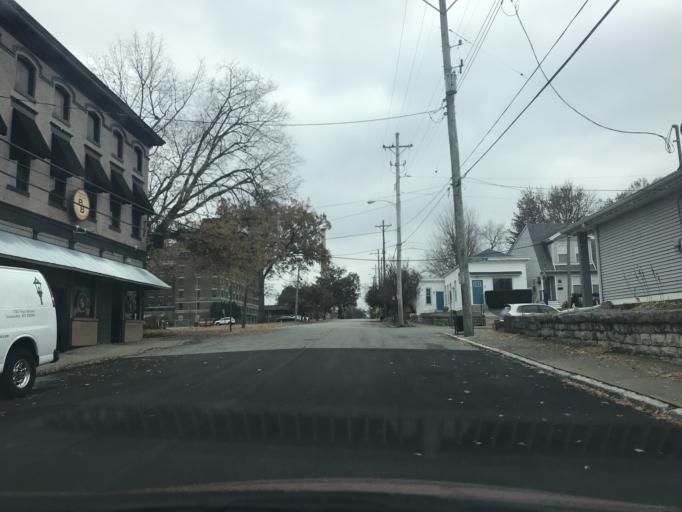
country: US
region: Kentucky
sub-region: Jefferson County
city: Louisville
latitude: 38.2417
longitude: -85.7346
